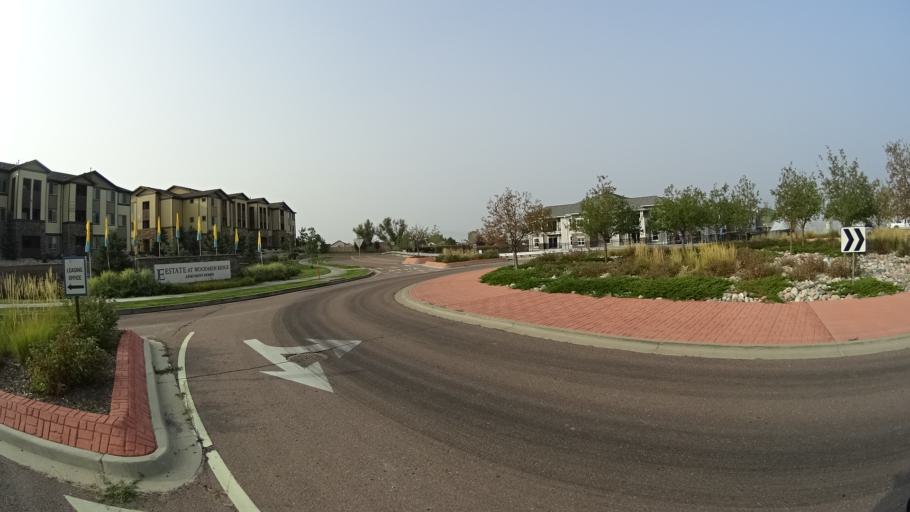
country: US
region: Colorado
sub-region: El Paso County
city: Black Forest
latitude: 38.9386
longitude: -104.7244
